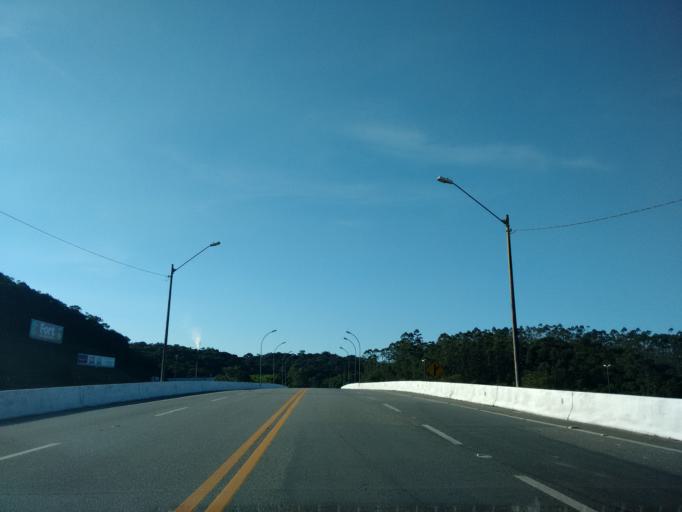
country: BR
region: Santa Catarina
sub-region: Joinville
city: Joinville
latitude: -26.4383
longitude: -48.8064
